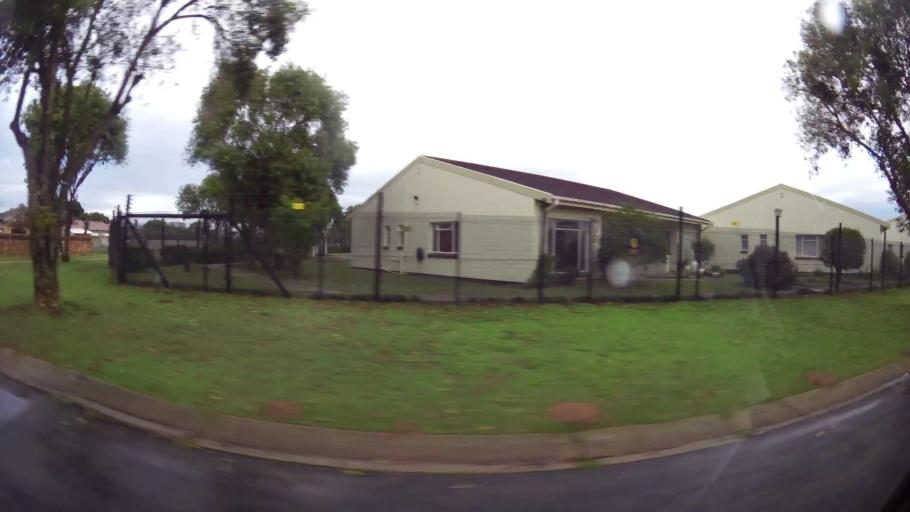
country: ZA
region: Eastern Cape
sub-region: Nelson Mandela Bay Metropolitan Municipality
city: Port Elizabeth
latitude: -33.9850
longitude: 25.5642
